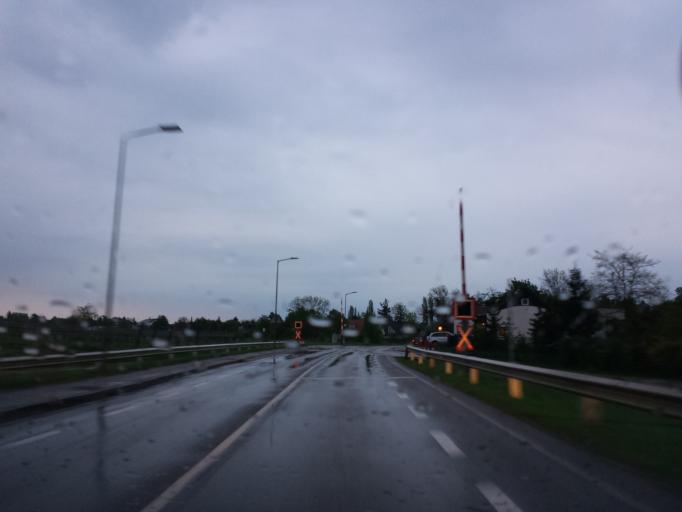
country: AT
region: Lower Austria
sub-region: Politischer Bezirk Modling
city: Perchtoldsdorf
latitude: 48.1274
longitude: 16.2626
